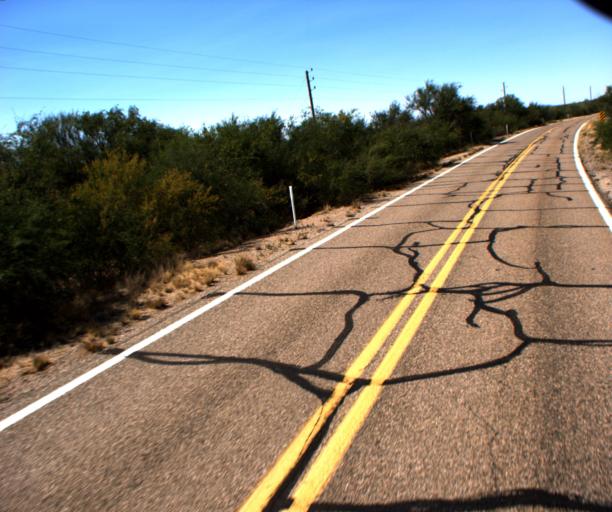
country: US
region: Arizona
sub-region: Pima County
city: Three Points
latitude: 31.8614
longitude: -111.3986
